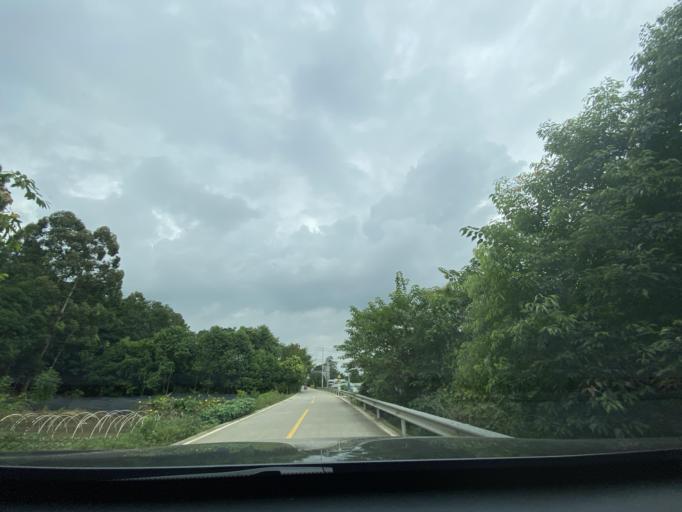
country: CN
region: Sichuan
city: Wujin
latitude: 30.3933
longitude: 103.9669
